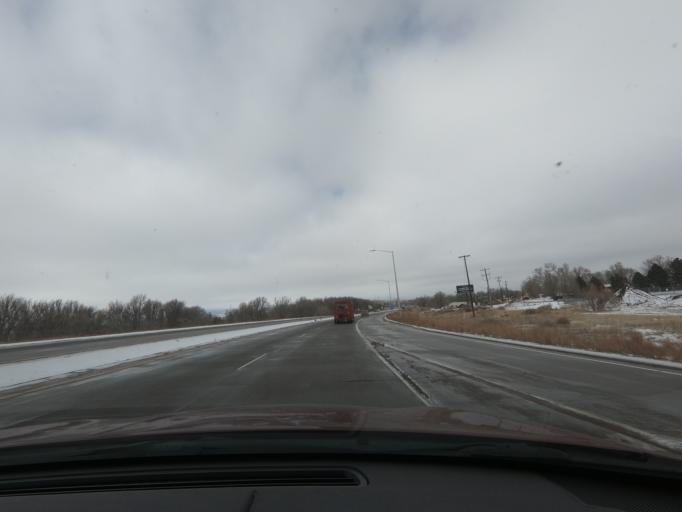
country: US
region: Colorado
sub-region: El Paso County
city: Security-Widefield
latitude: 38.7235
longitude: -104.7234
